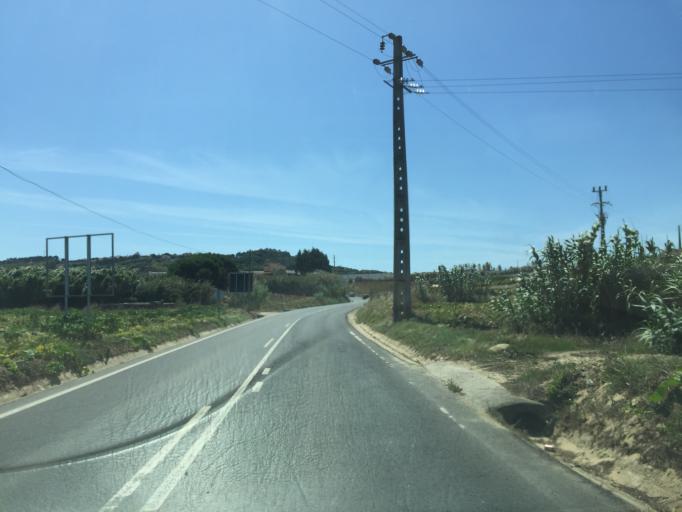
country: PT
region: Lisbon
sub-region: Lourinha
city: Lourinha
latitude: 39.2325
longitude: -9.3130
